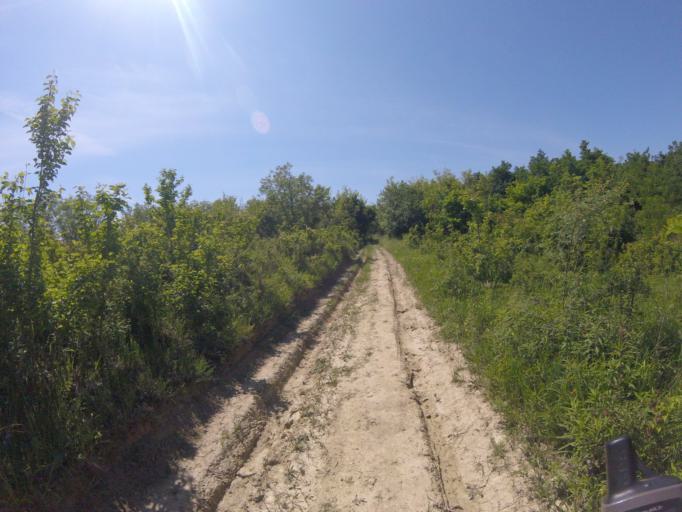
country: HU
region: Zala
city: Zalaszentgrot
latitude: 46.9247
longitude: 17.0454
